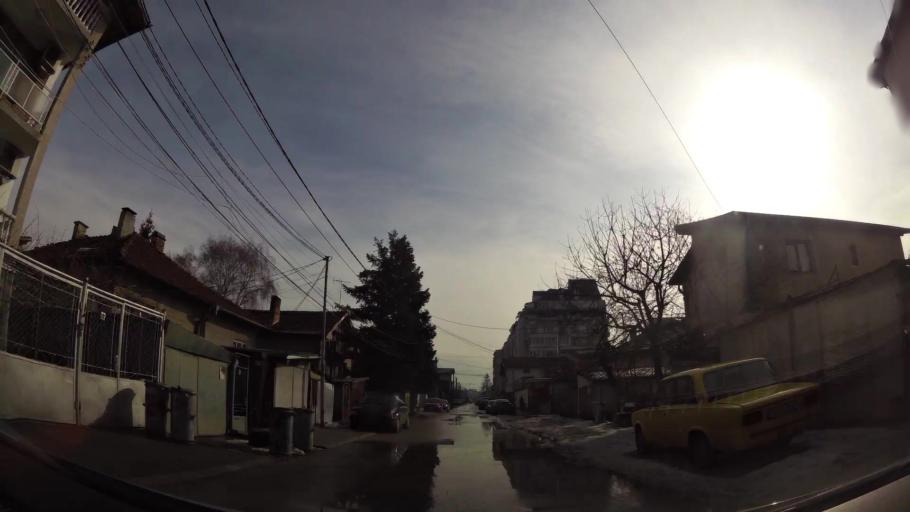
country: BG
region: Sofia-Capital
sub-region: Stolichna Obshtina
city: Sofia
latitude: 42.7229
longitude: 23.2656
